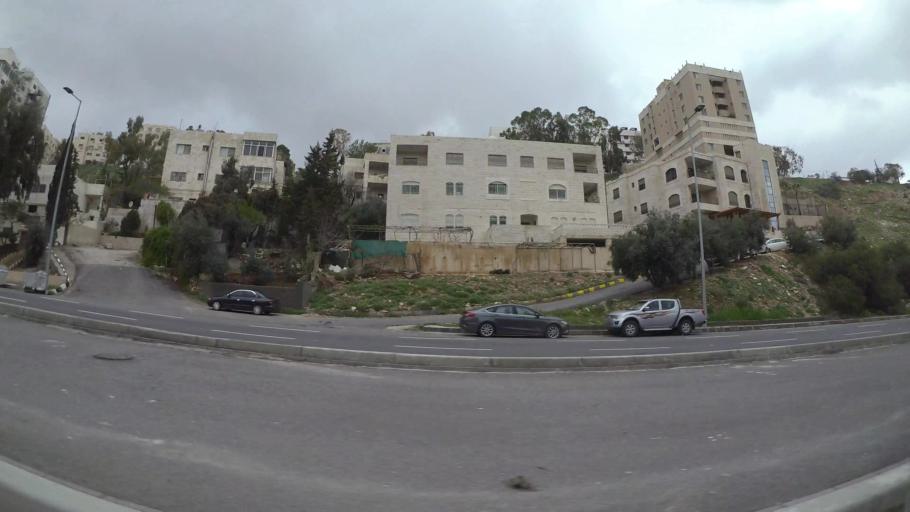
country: JO
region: Amman
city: Amman
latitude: 31.9497
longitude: 35.9022
